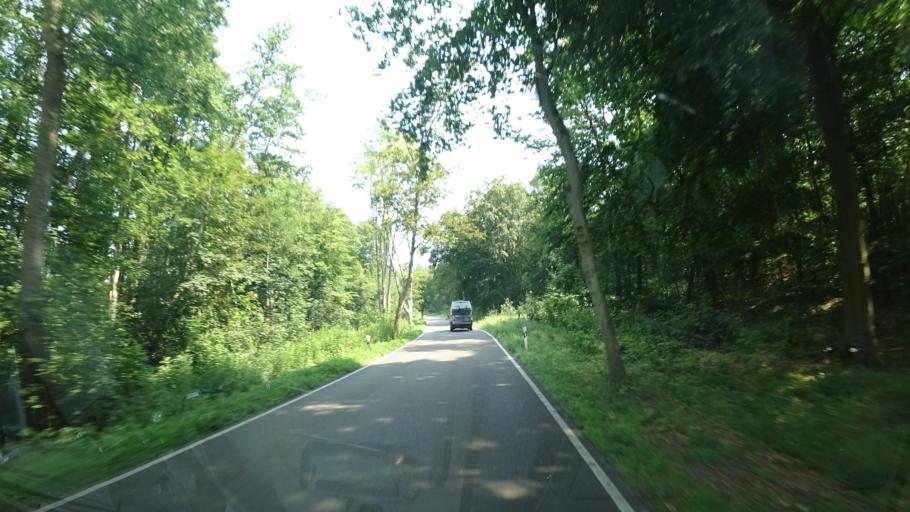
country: PL
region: West Pomeranian Voivodeship
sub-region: Swinoujscie
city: Swinoujscie
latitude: 53.8907
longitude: 14.1925
